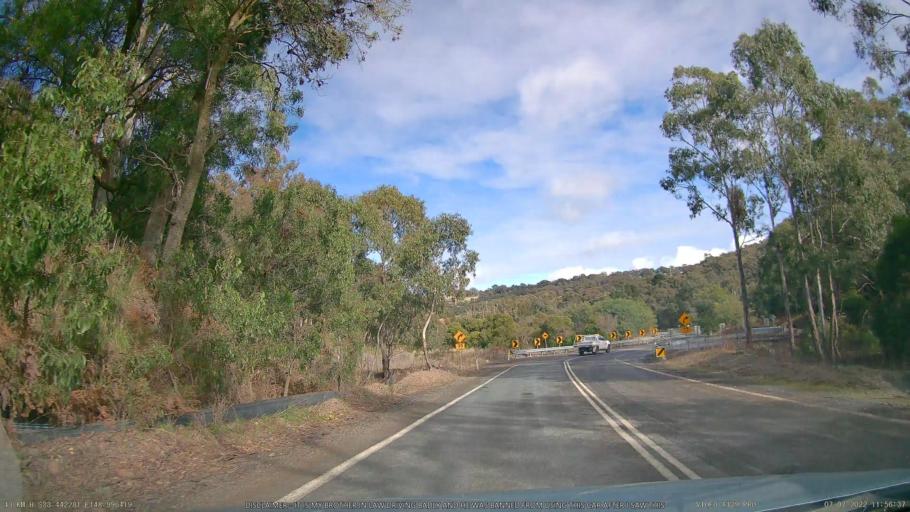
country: AU
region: New South Wales
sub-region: Blayney
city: Millthorpe
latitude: -33.4424
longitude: 148.9961
